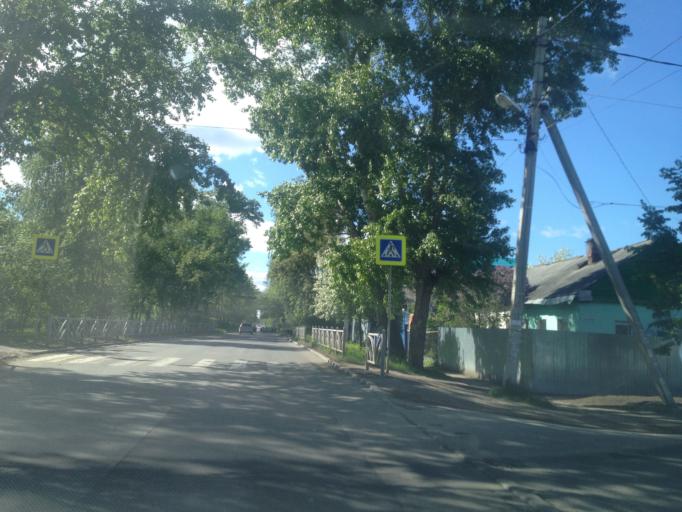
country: RU
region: Sverdlovsk
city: Sovkhoznyy
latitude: 56.8027
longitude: 60.5833
